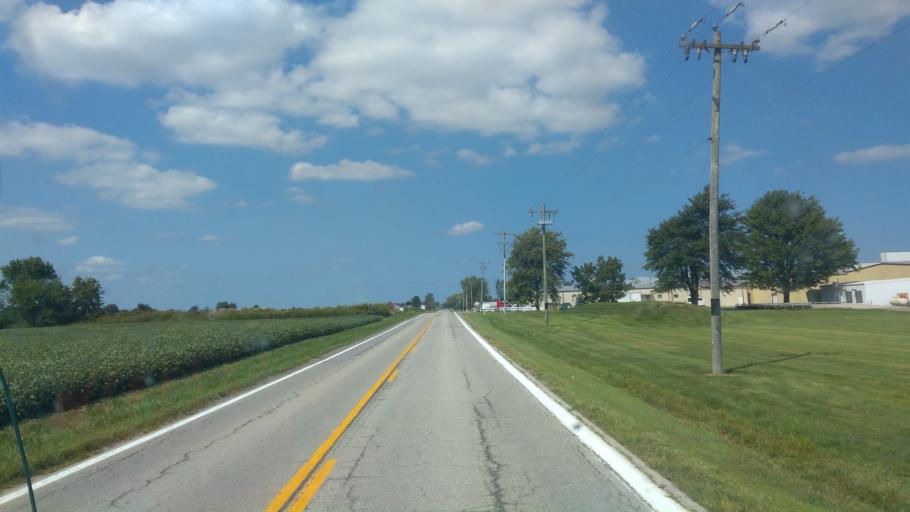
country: US
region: Ohio
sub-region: Union County
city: Richwood
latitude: 40.3918
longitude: -83.4536
